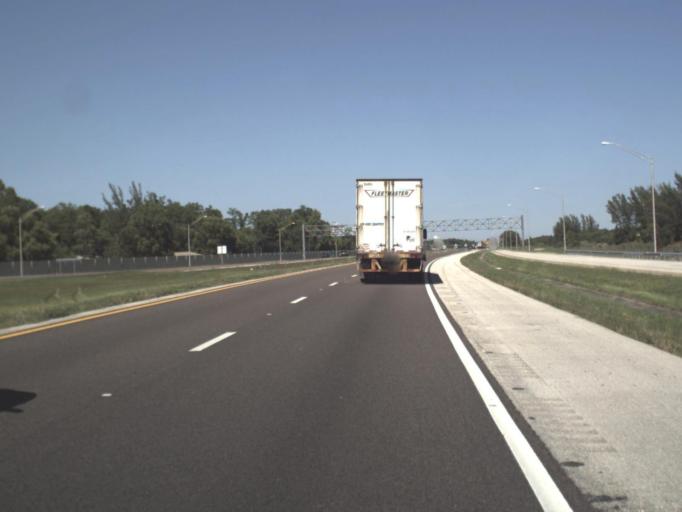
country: US
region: Florida
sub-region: Collier County
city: Golden Gate
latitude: 26.1780
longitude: -81.7352
